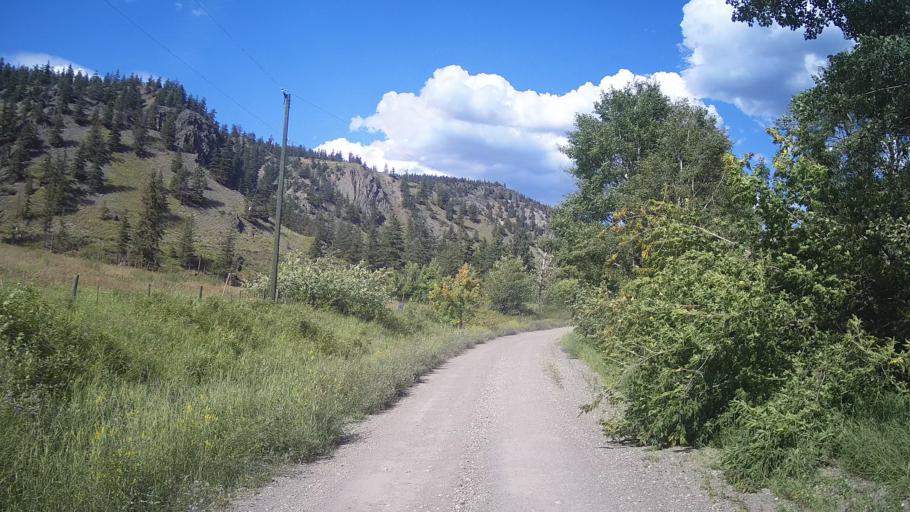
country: CA
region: British Columbia
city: Lillooet
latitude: 51.2376
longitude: -122.0476
